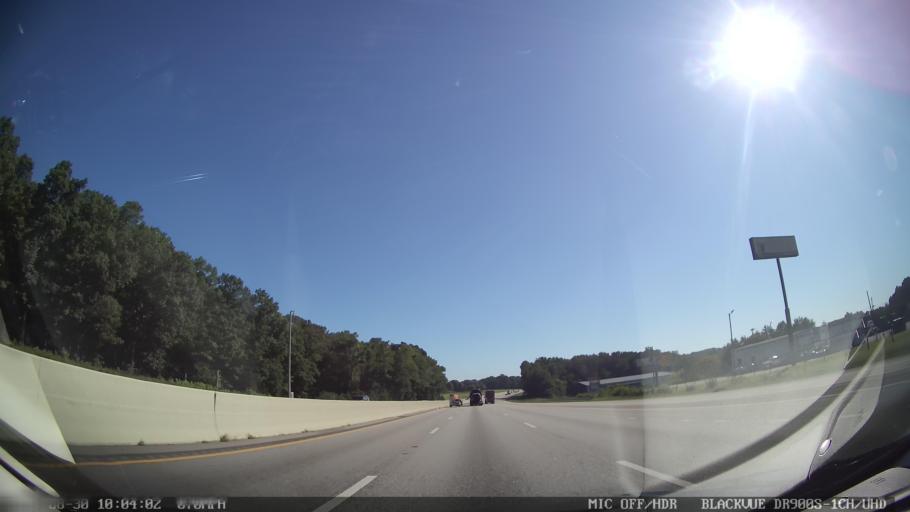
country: US
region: South Carolina
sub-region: Spartanburg County
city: Duncan
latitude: 34.8975
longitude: -82.1542
